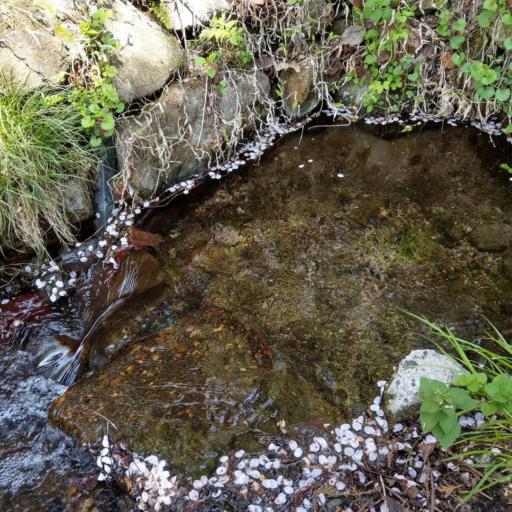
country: JP
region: Nagano
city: Komoro
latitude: 36.3364
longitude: 138.5027
